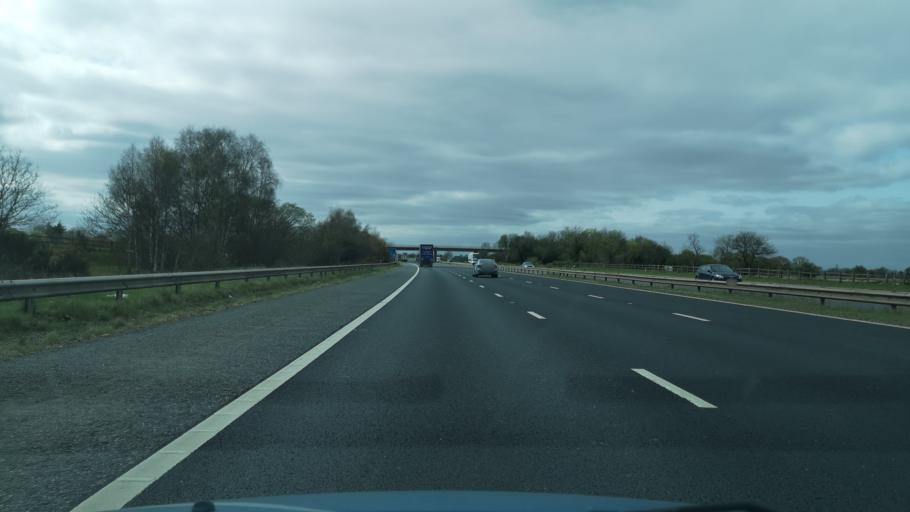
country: GB
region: England
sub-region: East Riding of Yorkshire
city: Pollington
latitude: 53.6949
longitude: -1.1312
